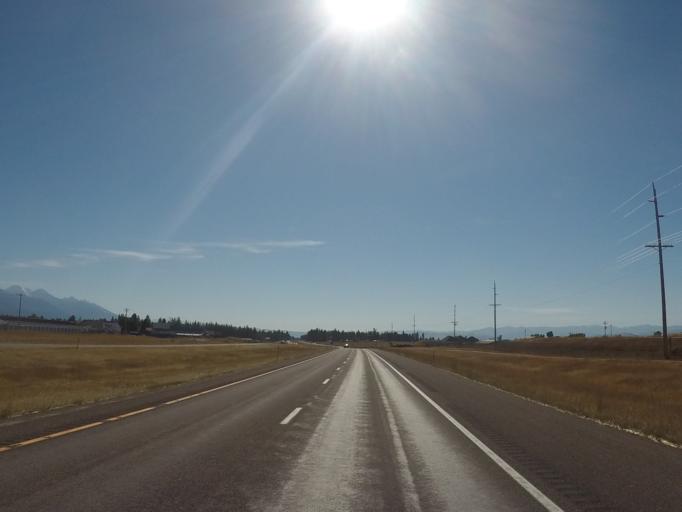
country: US
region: Montana
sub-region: Lake County
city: Pablo
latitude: 47.6406
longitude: -114.1139
